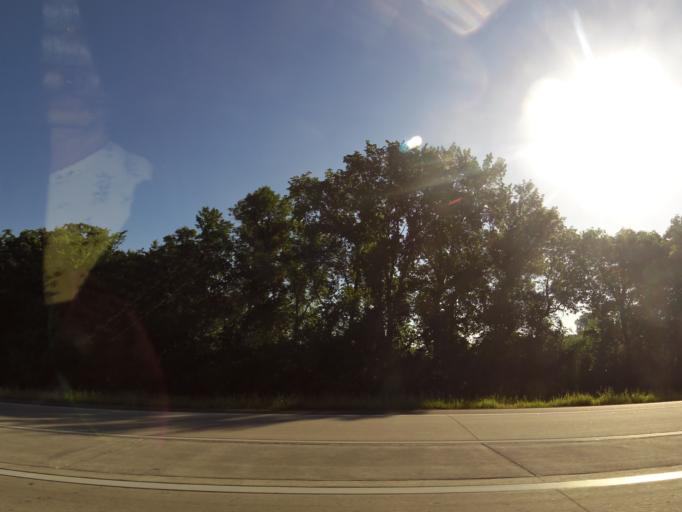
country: US
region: Minnesota
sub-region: Stearns County
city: Saint Joseph
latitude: 45.5552
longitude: -94.3359
